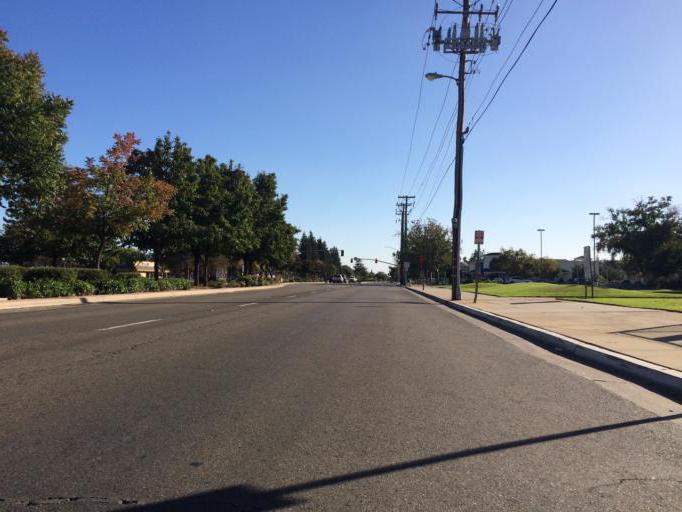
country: US
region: California
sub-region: Fresno County
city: Tarpey Village
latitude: 36.8099
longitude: -119.6821
